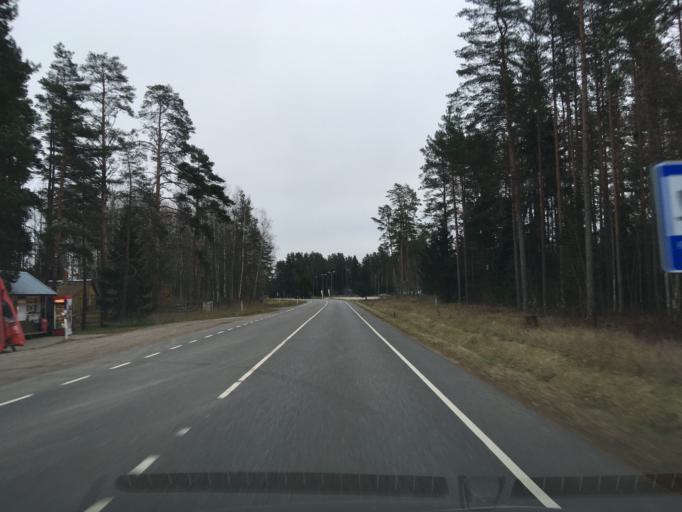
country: EE
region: Laeaene-Virumaa
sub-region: Kadrina vald
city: Kadrina
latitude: 59.4531
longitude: 26.0265
